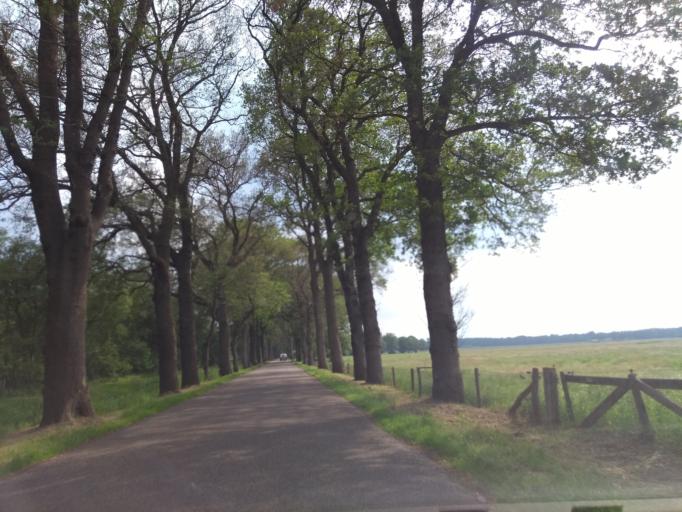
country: NL
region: Overijssel
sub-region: Gemeente Staphorst
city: Staphorst
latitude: 52.6504
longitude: 6.2915
